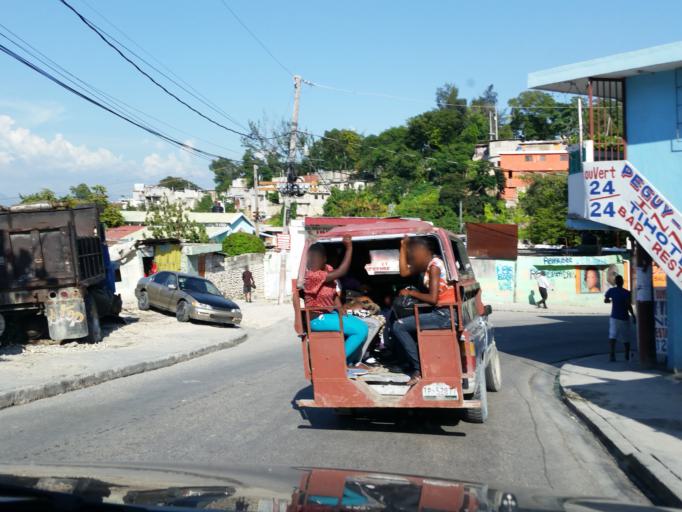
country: HT
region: Ouest
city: Petionville
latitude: 18.5169
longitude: -72.2812
